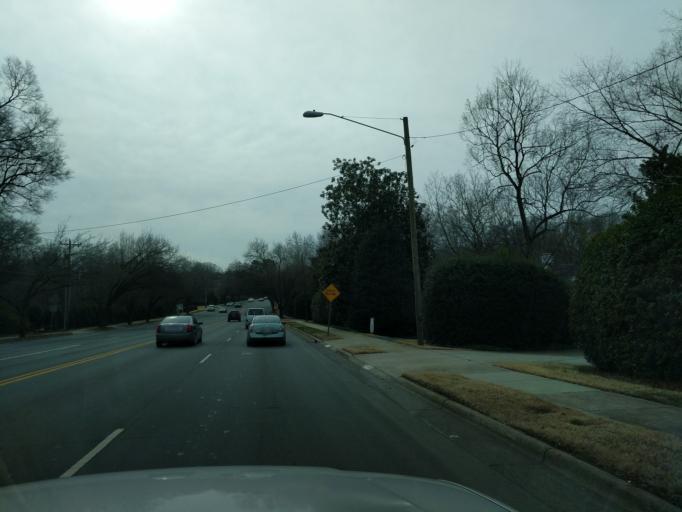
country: US
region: North Carolina
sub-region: Mecklenburg County
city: Charlotte
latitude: 35.1716
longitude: -80.8230
